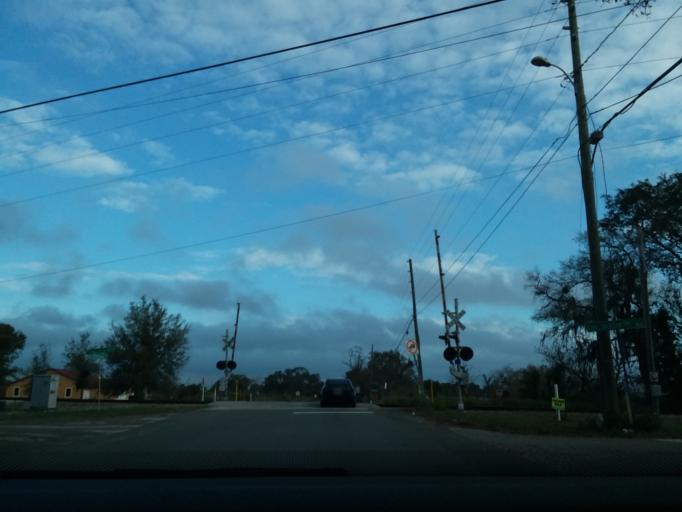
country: US
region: Florida
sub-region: Polk County
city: Haines City
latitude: 28.1107
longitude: -81.6481
